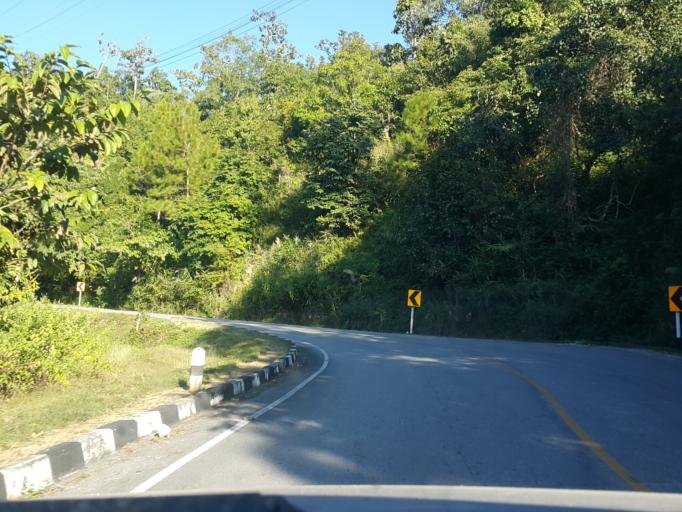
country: TH
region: Mae Hong Son
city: Mae Hi
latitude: 19.2674
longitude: 98.5207
